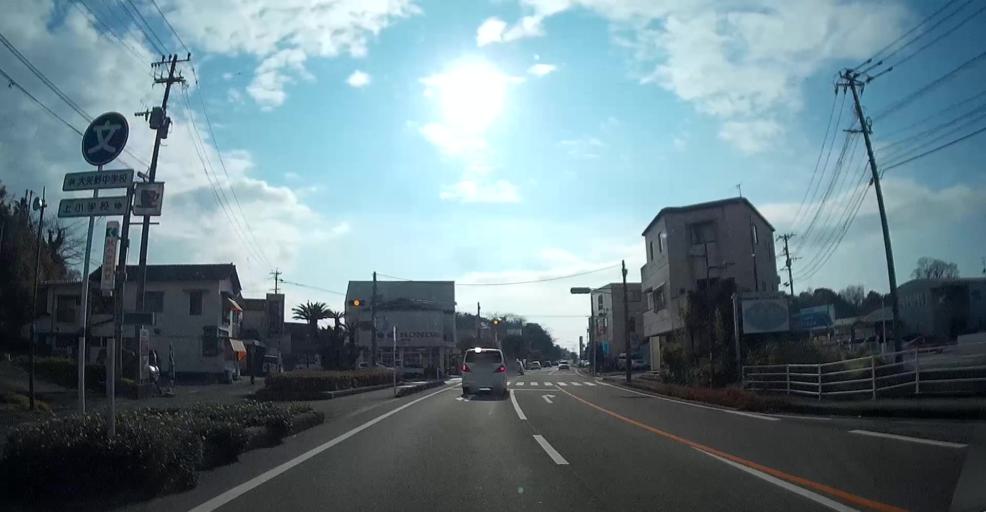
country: JP
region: Kumamoto
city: Yatsushiro
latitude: 32.5842
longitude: 130.4290
